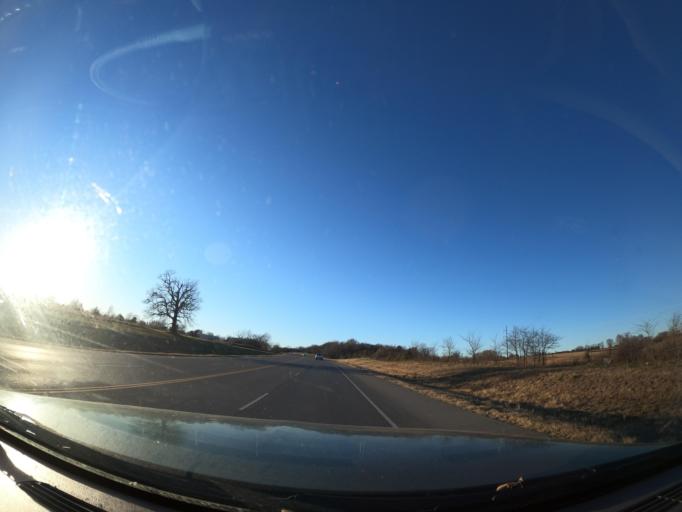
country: US
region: Oklahoma
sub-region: Pittsburg County
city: Hartshorne
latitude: 34.8933
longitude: -95.6261
